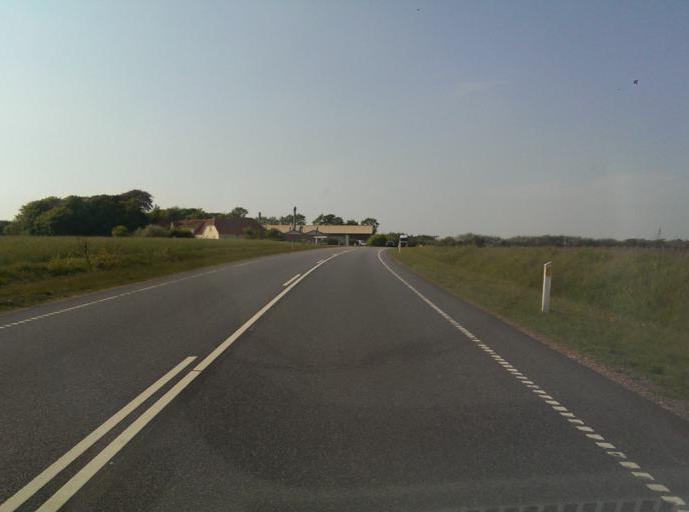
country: DK
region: South Denmark
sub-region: Esbjerg Kommune
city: Tjaereborg
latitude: 55.5071
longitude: 8.5984
